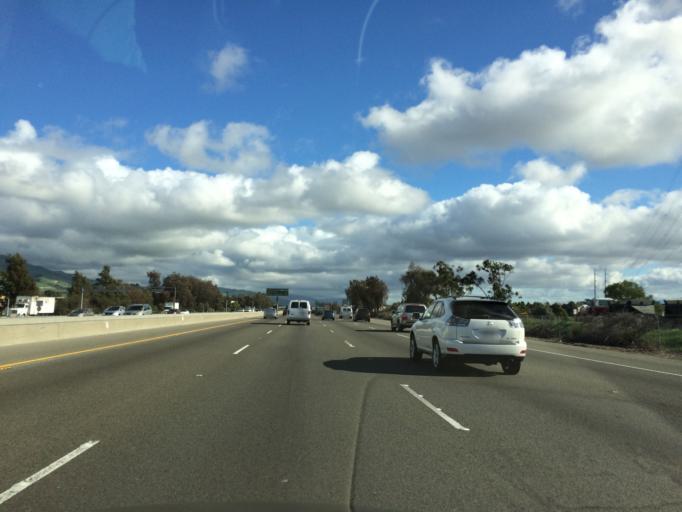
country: US
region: California
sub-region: Alameda County
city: Fremont
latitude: 37.5003
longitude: -121.9584
